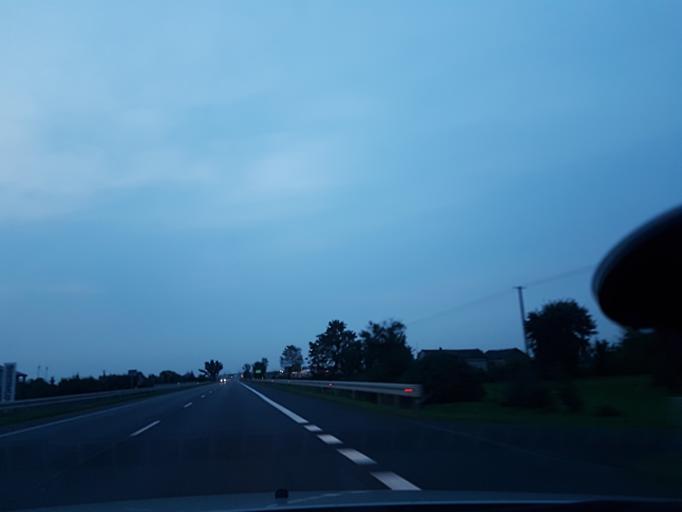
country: PL
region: Lodz Voivodeship
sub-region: Powiat kutnowski
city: Krzyzanow
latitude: 52.2209
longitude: 19.4520
